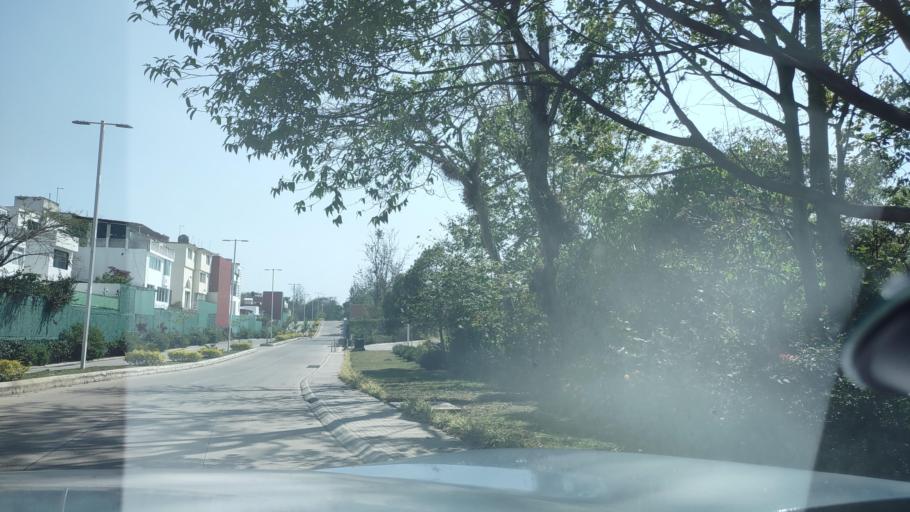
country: MX
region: Veracruz
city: El Castillo
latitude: 19.5256
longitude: -96.8689
